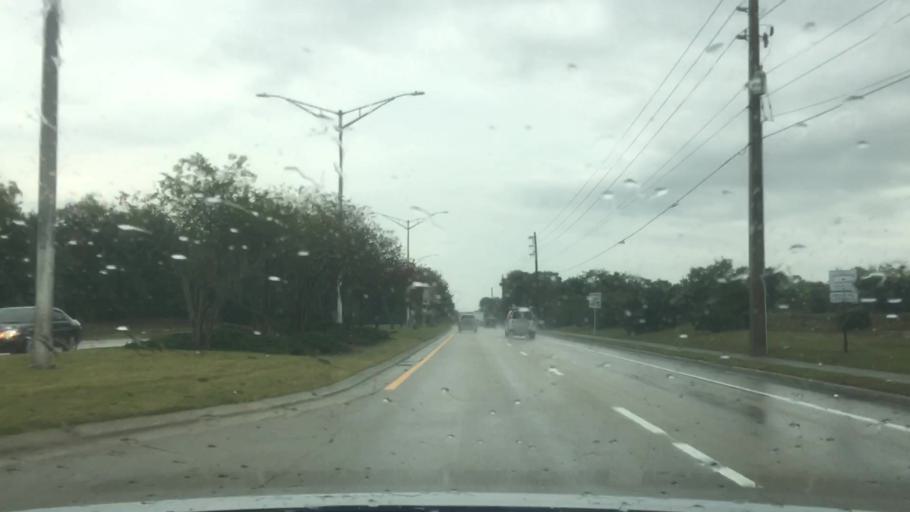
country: US
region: Florida
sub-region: Duval County
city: Atlantic Beach
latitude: 30.3479
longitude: -81.5233
